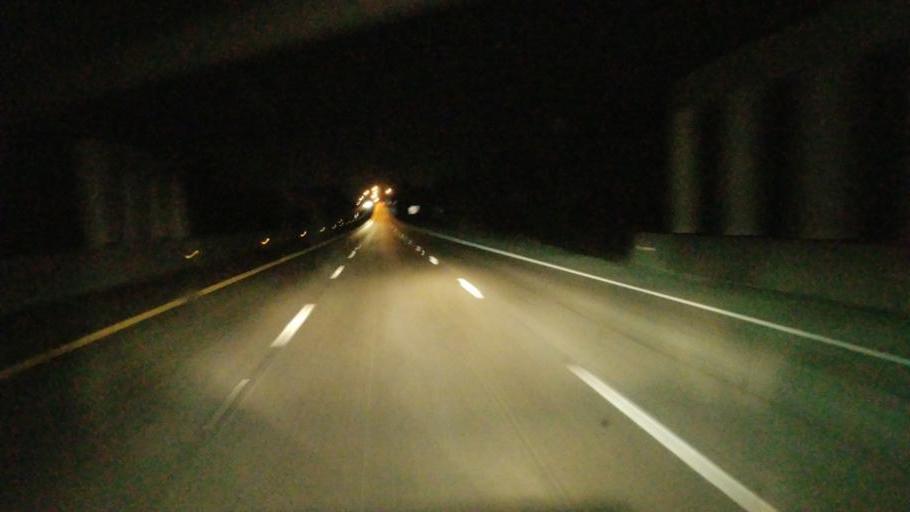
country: US
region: Ohio
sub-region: Clark County
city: Park Layne
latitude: 39.8666
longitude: -84.0790
